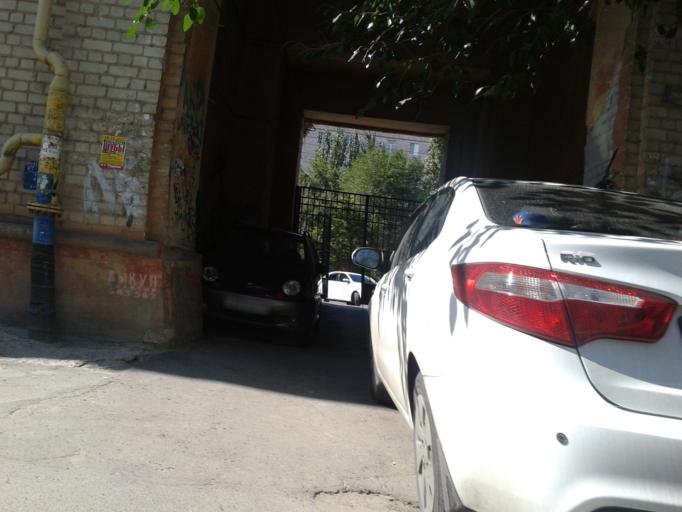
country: RU
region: Volgograd
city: Volgograd
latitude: 48.7098
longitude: 44.5224
